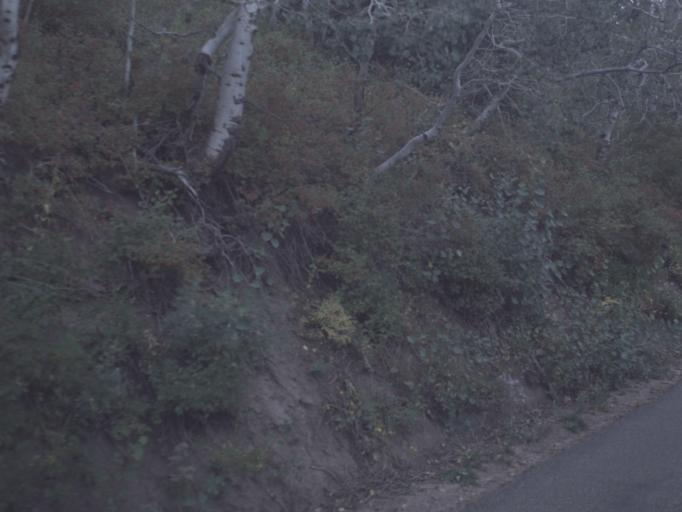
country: US
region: Utah
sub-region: Utah County
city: Lindon
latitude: 40.4405
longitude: -111.6211
